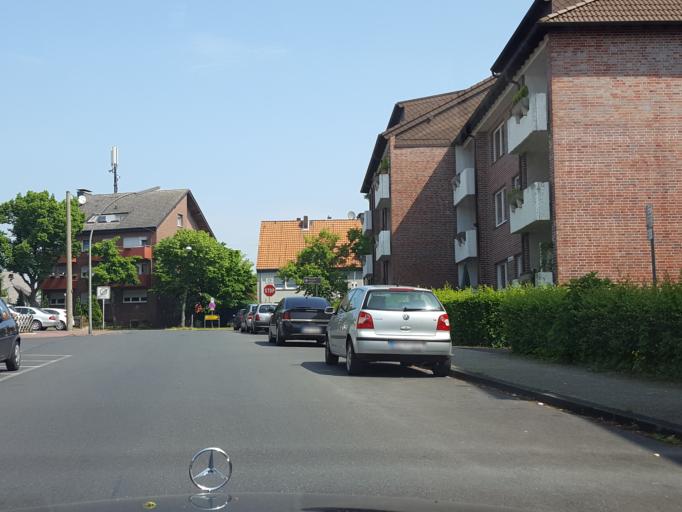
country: DE
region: North Rhine-Westphalia
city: Oer-Erkenschwick
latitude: 51.6411
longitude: 7.2771
